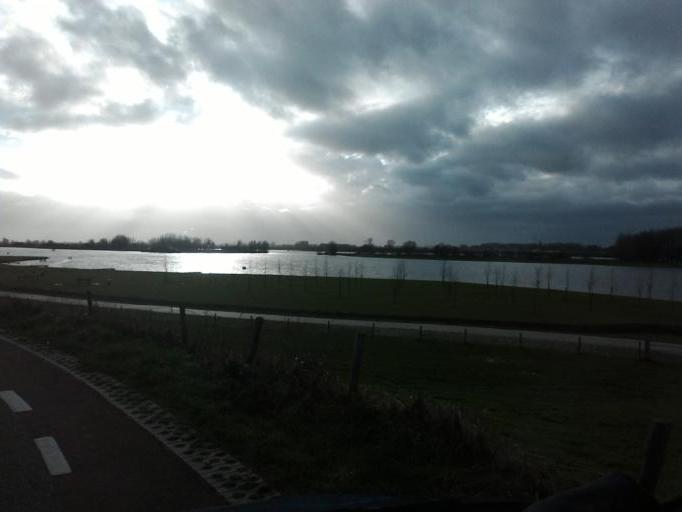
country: NL
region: Utrecht
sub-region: Gemeente Houten
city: Houten
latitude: 51.9895
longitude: 5.1503
